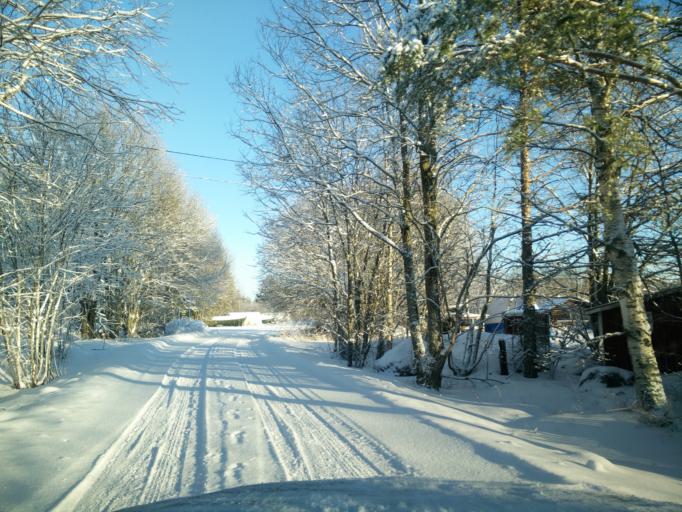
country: SE
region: Vaesternorrland
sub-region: Sundsvalls Kommun
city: Njurundabommen
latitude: 62.2322
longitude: 17.6556
